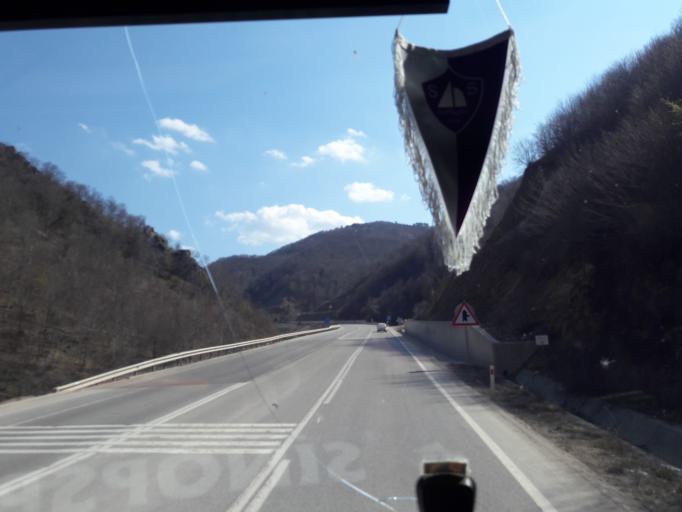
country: TR
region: Sinop
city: Erfelek
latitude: 41.6839
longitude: 34.9084
